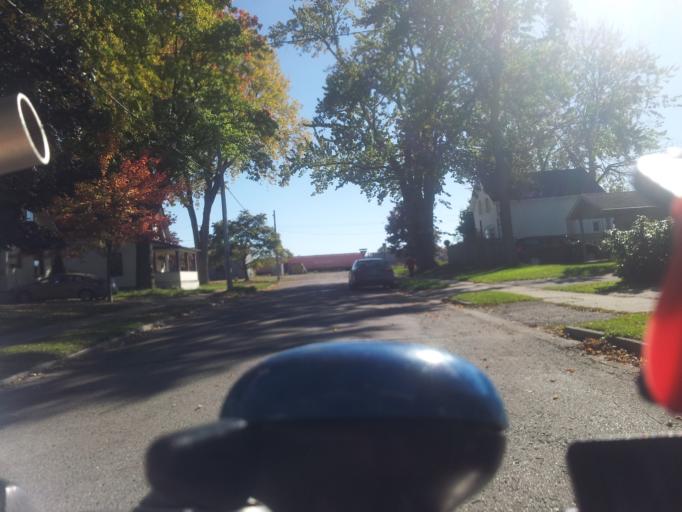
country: CA
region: Ontario
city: Stratford
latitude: 43.3657
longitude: -80.9702
